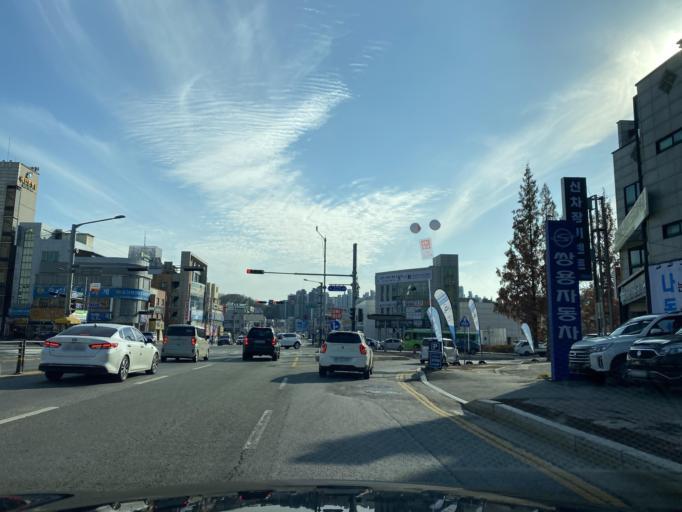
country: KR
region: Chungcheongnam-do
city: Cheonan
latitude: 36.7992
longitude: 127.1592
